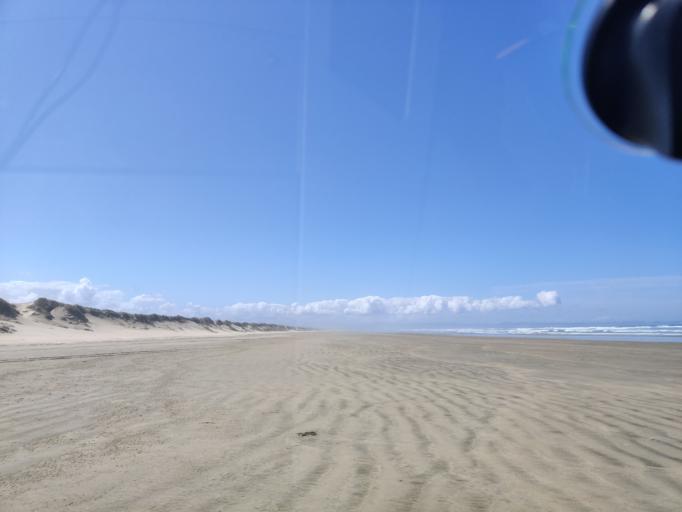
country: NZ
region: Northland
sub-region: Far North District
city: Kaitaia
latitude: -34.9268
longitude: 173.1055
